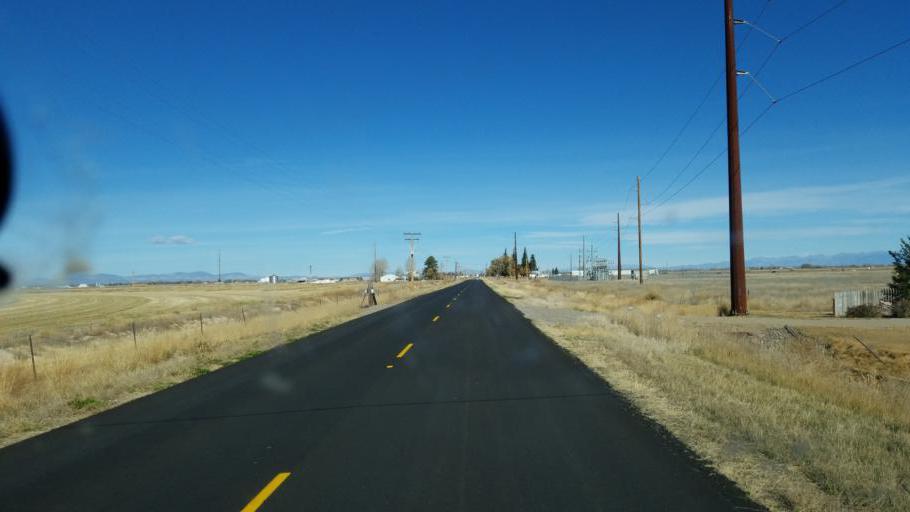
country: US
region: Colorado
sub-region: Rio Grande County
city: Monte Vista
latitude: 37.5425
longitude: -106.0942
